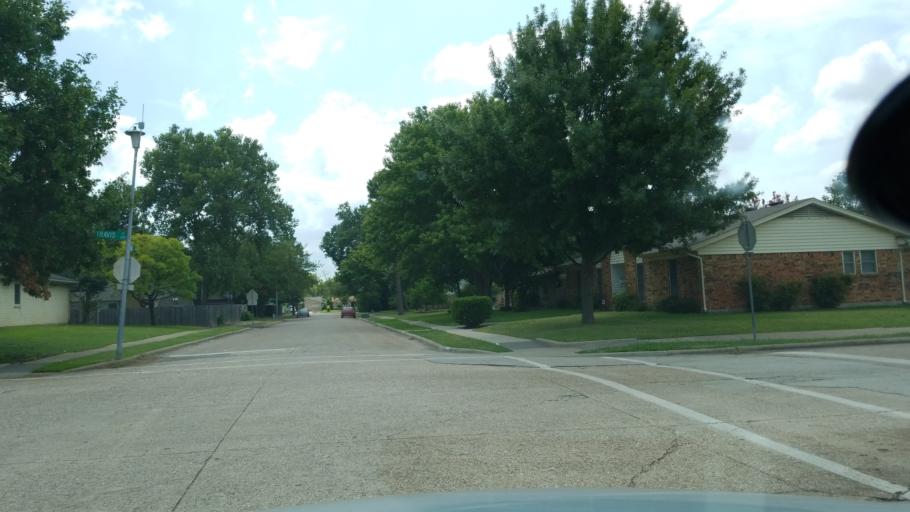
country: US
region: Texas
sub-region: Dallas County
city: Garland
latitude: 32.9244
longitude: -96.6529
